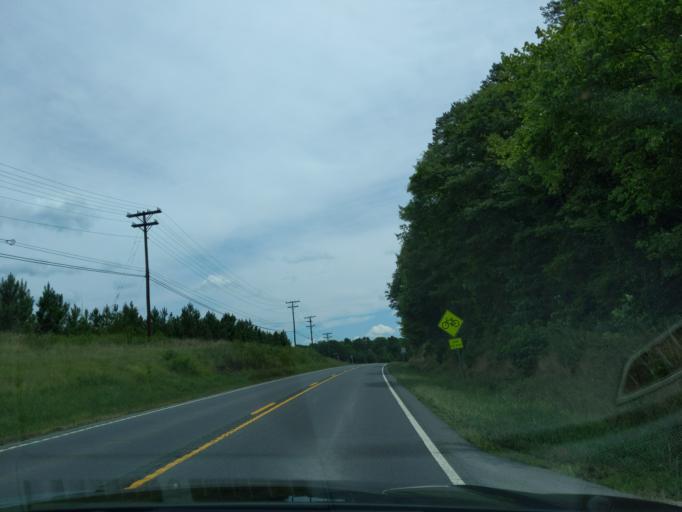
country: US
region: North Carolina
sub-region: Rowan County
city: Rockwell
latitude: 35.4680
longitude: -80.2895
